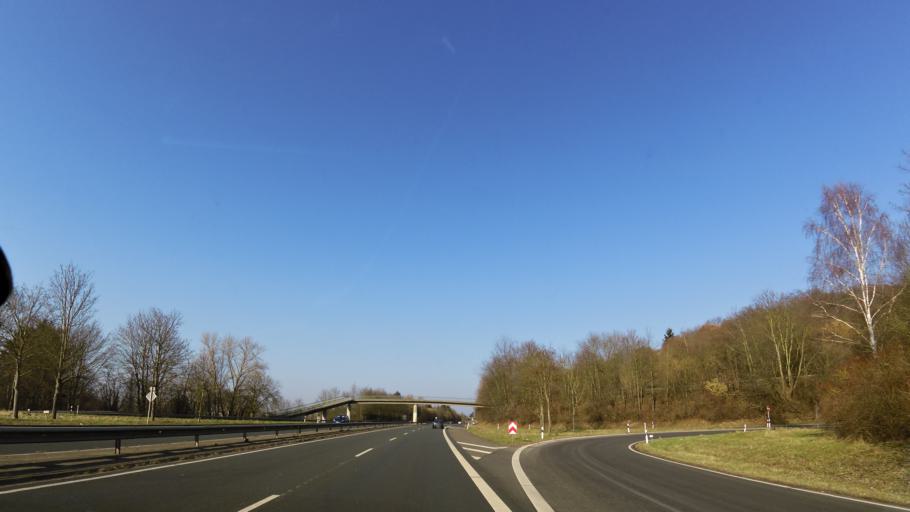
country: DE
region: Rheinland-Pfalz
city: Koblenz
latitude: 50.3359
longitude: 7.6057
